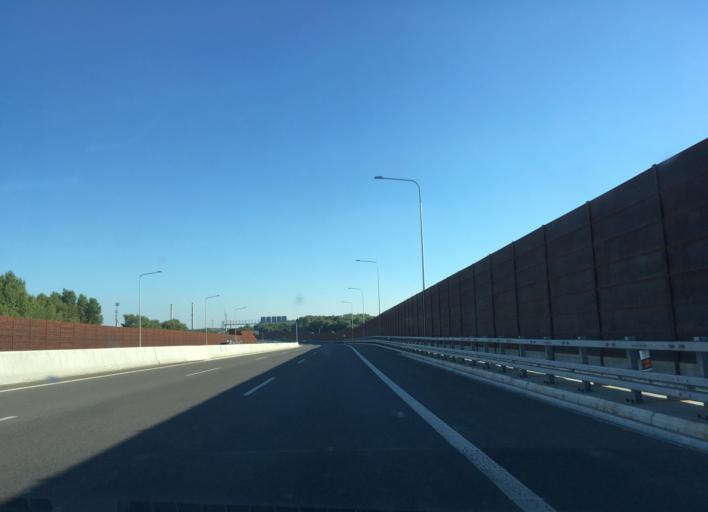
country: SK
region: Bratislavsky
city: Bratislava
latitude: 48.1293
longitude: 17.1619
